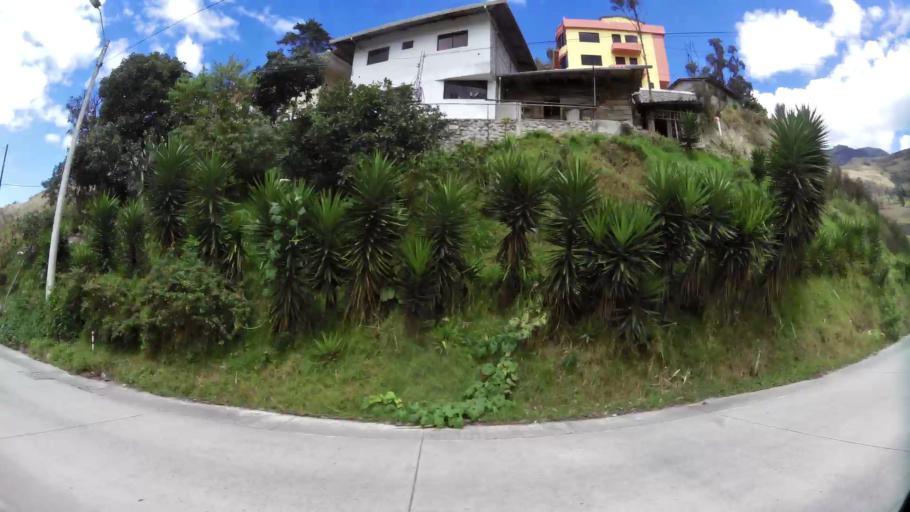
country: EC
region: Azuay
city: Cuenca
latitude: -3.1527
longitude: -79.1459
